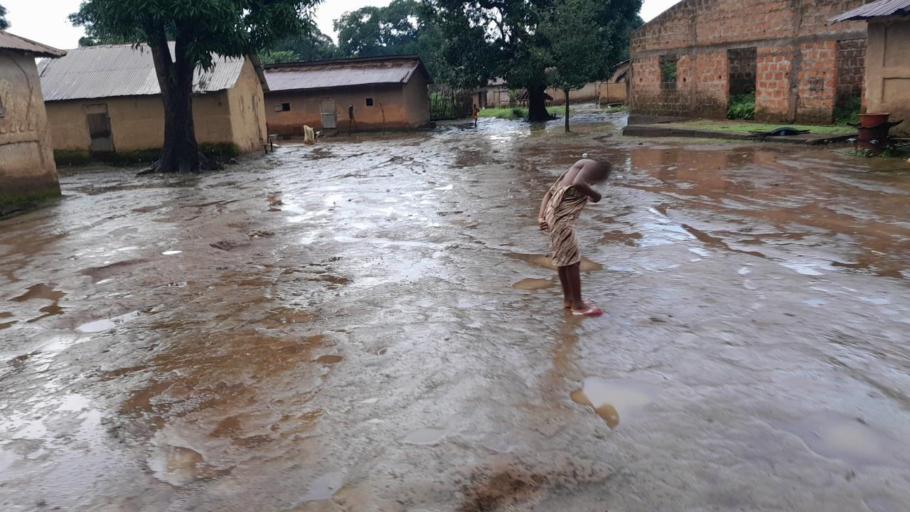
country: GN
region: Boke
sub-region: Boke Prefecture
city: Boke
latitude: 11.1588
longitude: -14.4171
